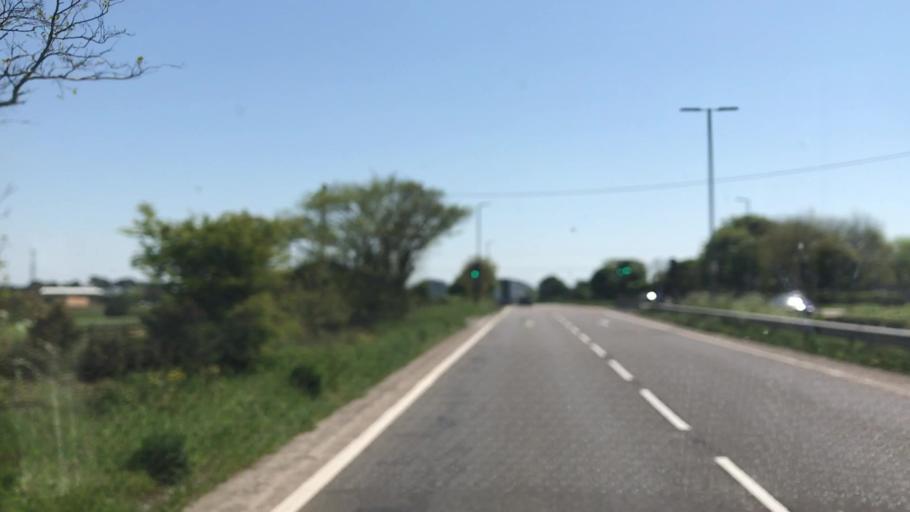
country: GB
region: England
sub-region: Cornwall
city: Truro
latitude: 50.2641
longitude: -5.1101
